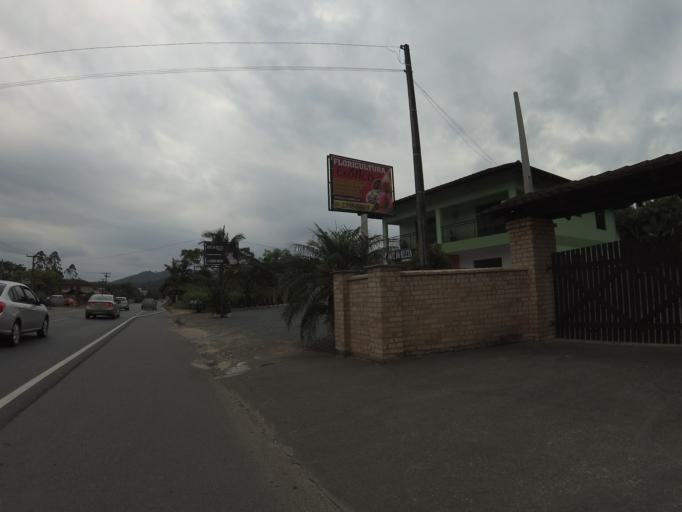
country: BR
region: Santa Catarina
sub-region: Pomerode
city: Pomerode
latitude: -26.8271
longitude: -49.1604
